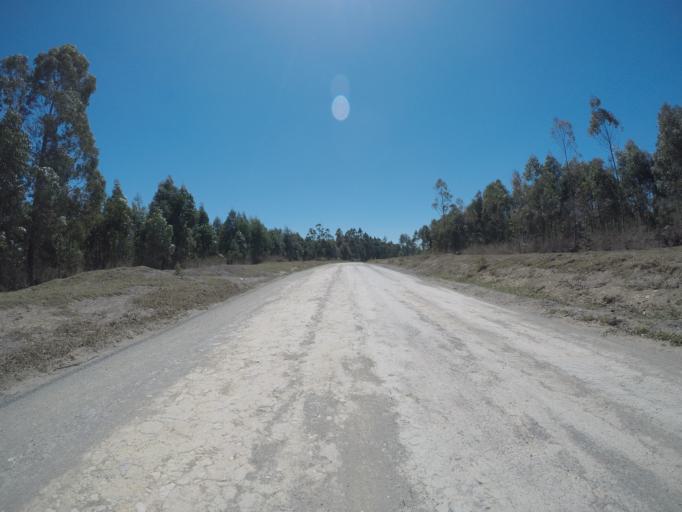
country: ZA
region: Eastern Cape
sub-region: OR Tambo District Municipality
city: Libode
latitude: -31.9538
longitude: 29.0233
